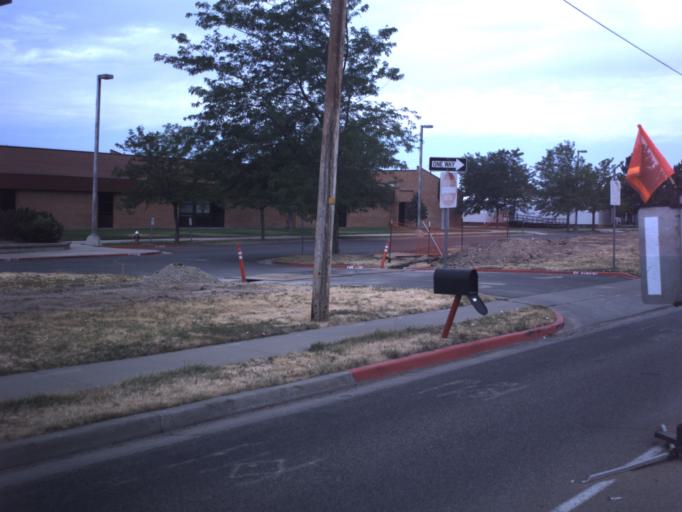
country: US
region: Utah
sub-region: Davis County
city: Syracuse
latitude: 41.0929
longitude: -112.0647
